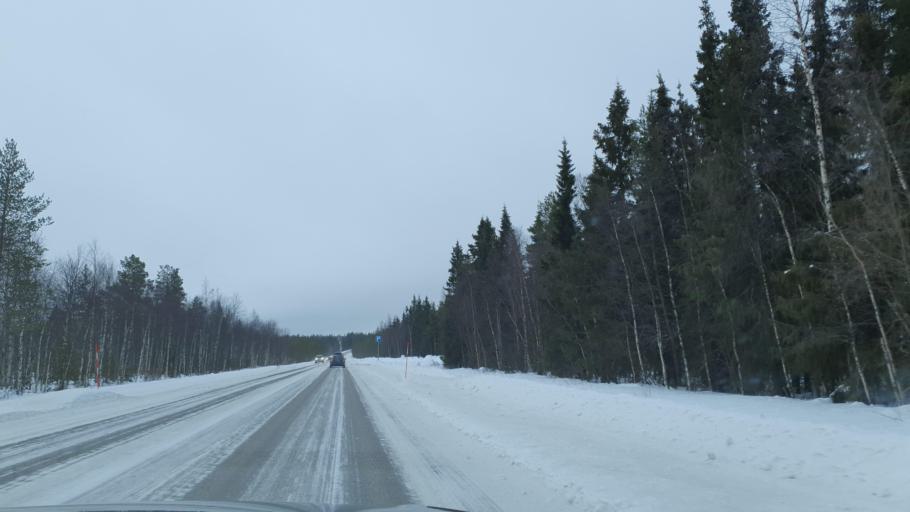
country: FI
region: Lapland
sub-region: Tunturi-Lappi
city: Kolari
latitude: 67.2864
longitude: 23.8536
